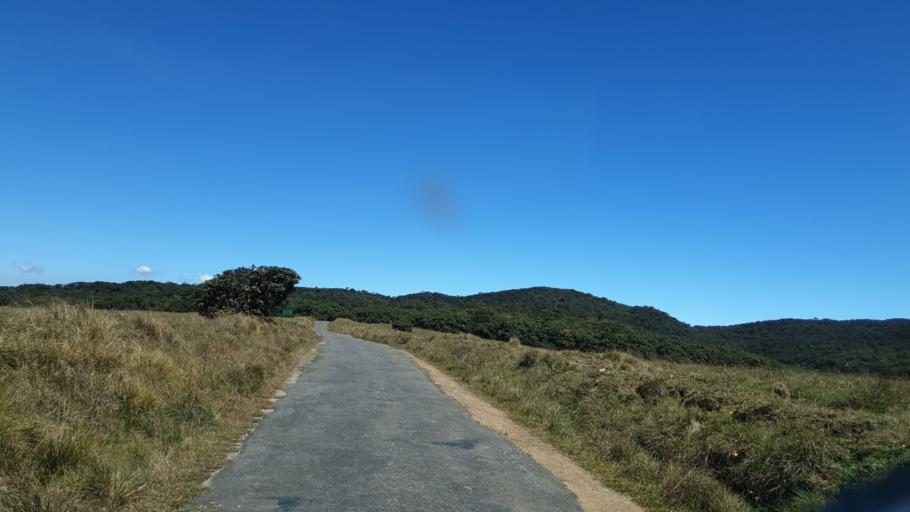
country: LK
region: Central
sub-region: Nuwara Eliya District
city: Nuwara Eliya
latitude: 6.8228
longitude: 80.8056
